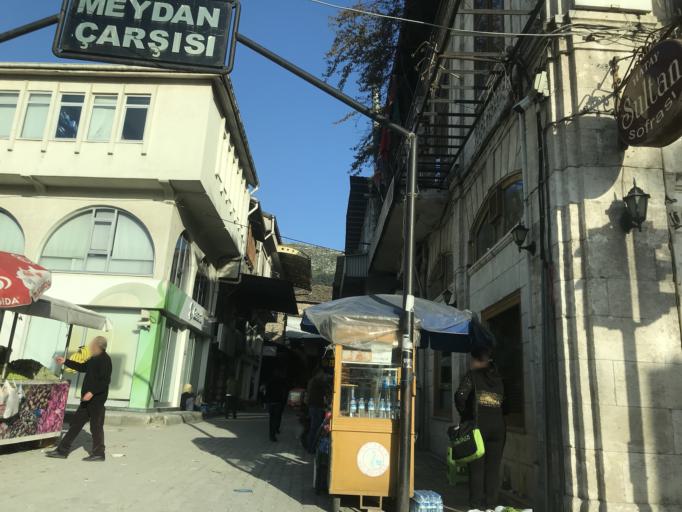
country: TR
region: Hatay
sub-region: Antakya Ilcesi
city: Antakya
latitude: 36.2043
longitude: 36.1622
